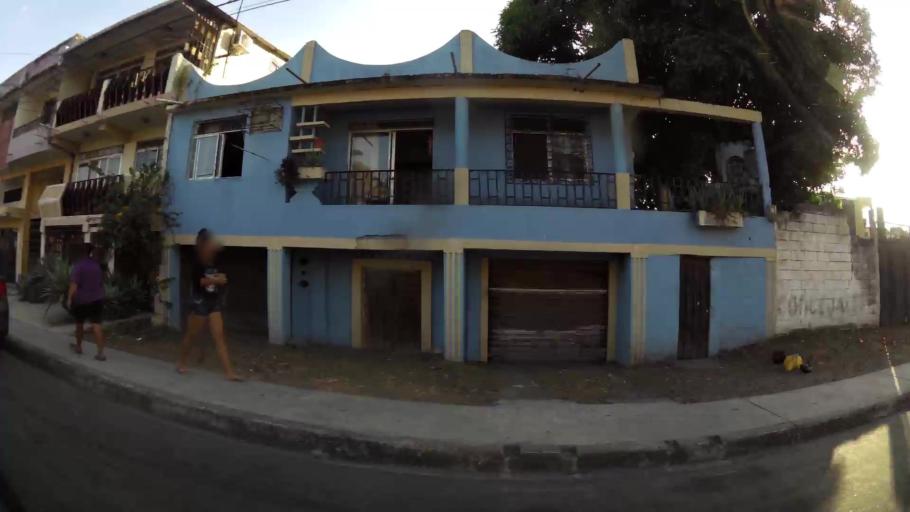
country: EC
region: Guayas
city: Eloy Alfaro
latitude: -2.1686
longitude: -79.8488
